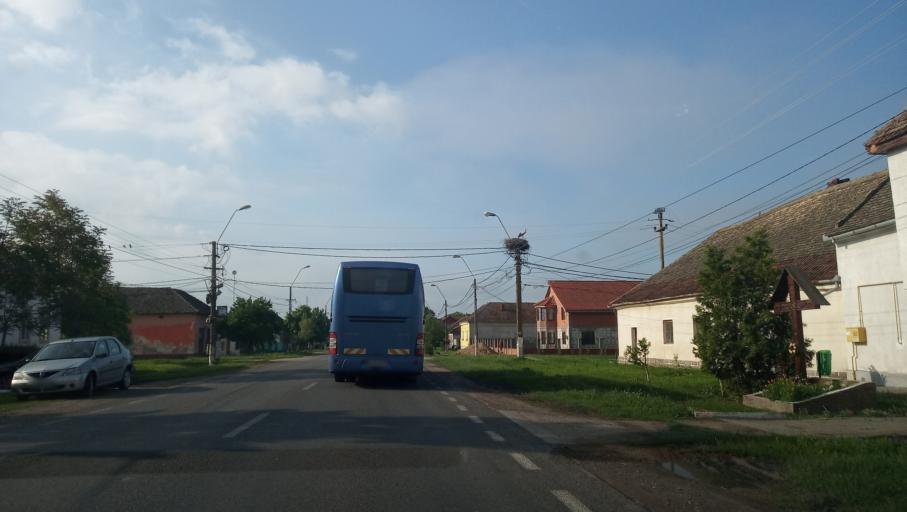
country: RO
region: Timis
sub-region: Comuna Moravita
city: Moravita
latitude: 45.2600
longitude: 21.2660
